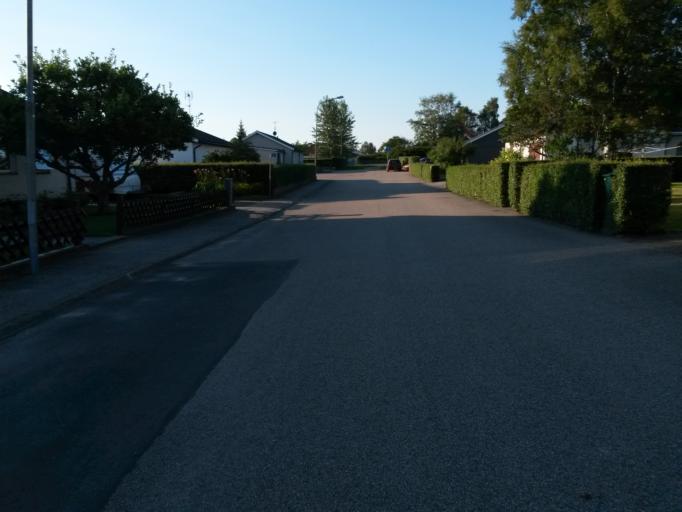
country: SE
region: Vaestra Goetaland
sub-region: Vargarda Kommun
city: Vargarda
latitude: 58.0239
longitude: 12.8121
